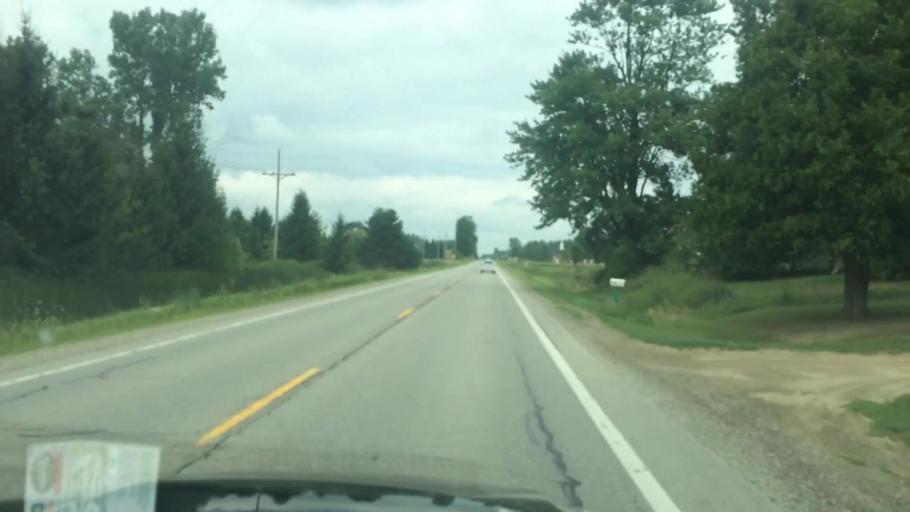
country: US
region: Michigan
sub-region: Sanilac County
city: Marlette
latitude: 43.4385
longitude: -83.0884
